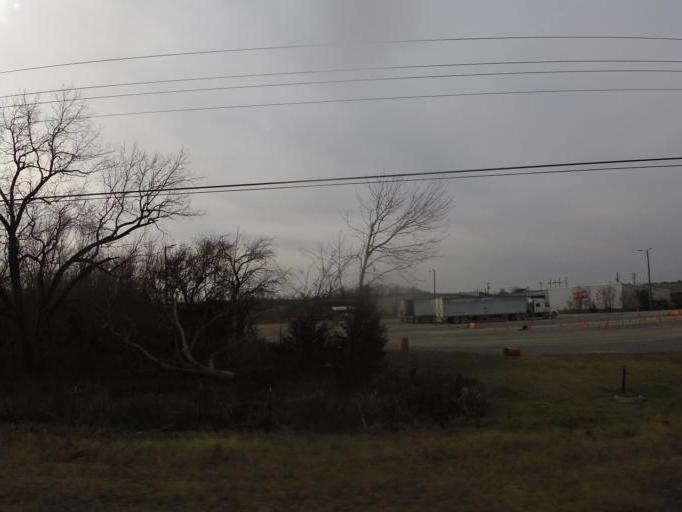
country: US
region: Alabama
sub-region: Montgomery County
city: Pike Road
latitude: 32.3010
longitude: -86.2046
